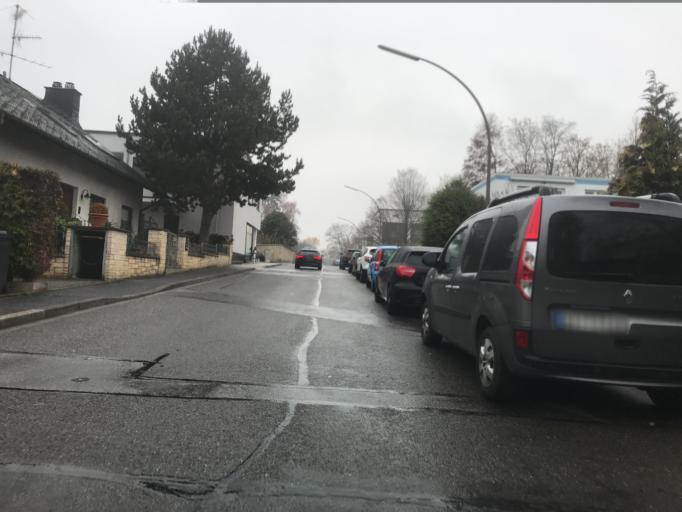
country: DE
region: Rheinland-Pfalz
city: Budenheim
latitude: 50.0452
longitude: 8.1851
